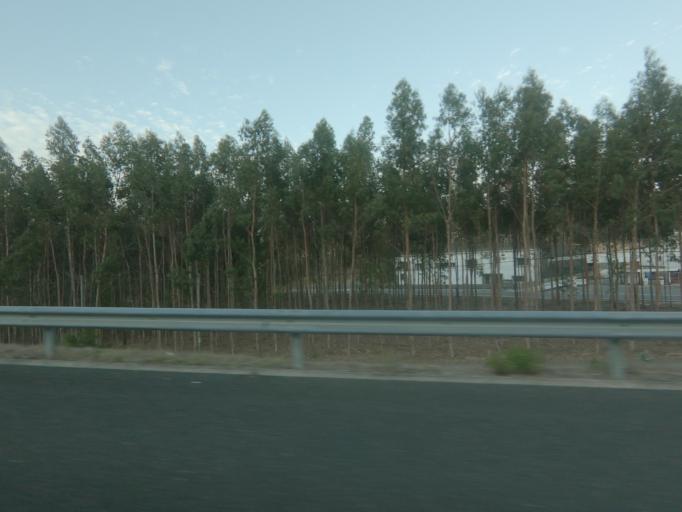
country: PT
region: Leiria
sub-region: Leiria
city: Caranguejeira
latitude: 39.7216
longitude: -8.7146
